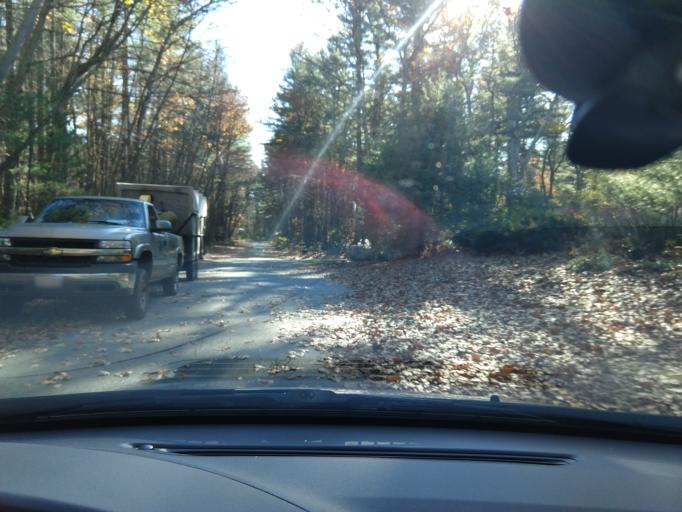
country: US
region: Massachusetts
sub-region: Middlesex County
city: Carlisle
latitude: 42.5104
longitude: -71.3339
